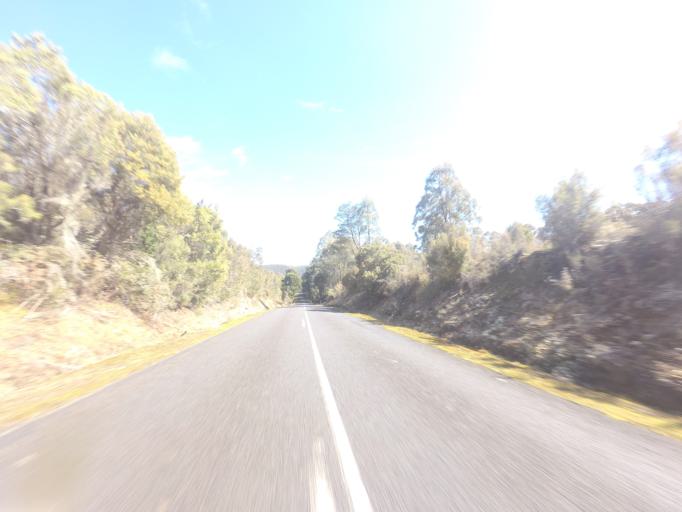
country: AU
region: Tasmania
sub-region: Derwent Valley
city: New Norfolk
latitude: -42.7610
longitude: 146.5319
